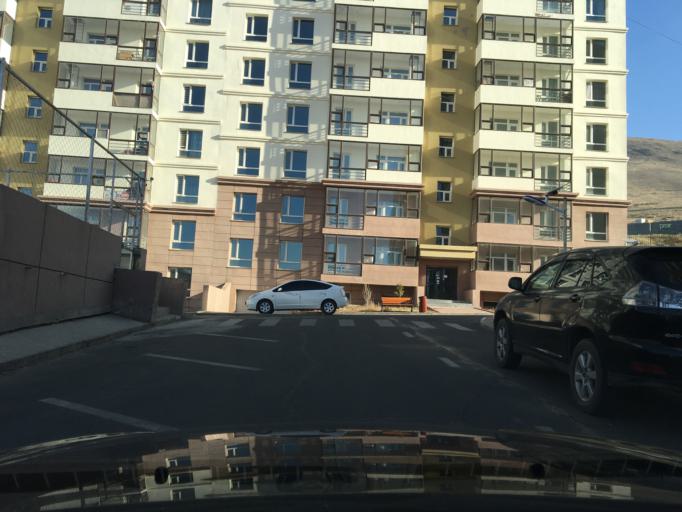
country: MN
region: Ulaanbaatar
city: Ulaanbaatar
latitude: 47.8755
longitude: 106.9177
